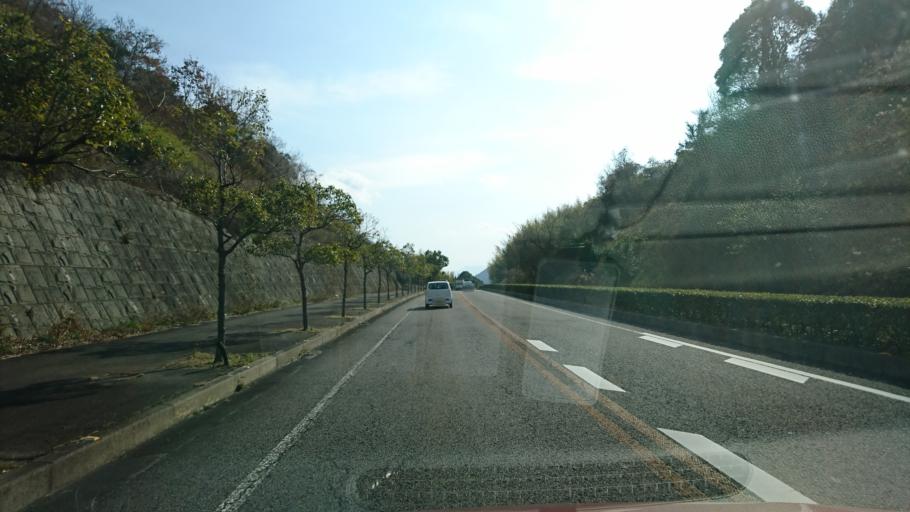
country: JP
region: Ehime
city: Saijo
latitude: 34.0147
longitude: 133.0328
